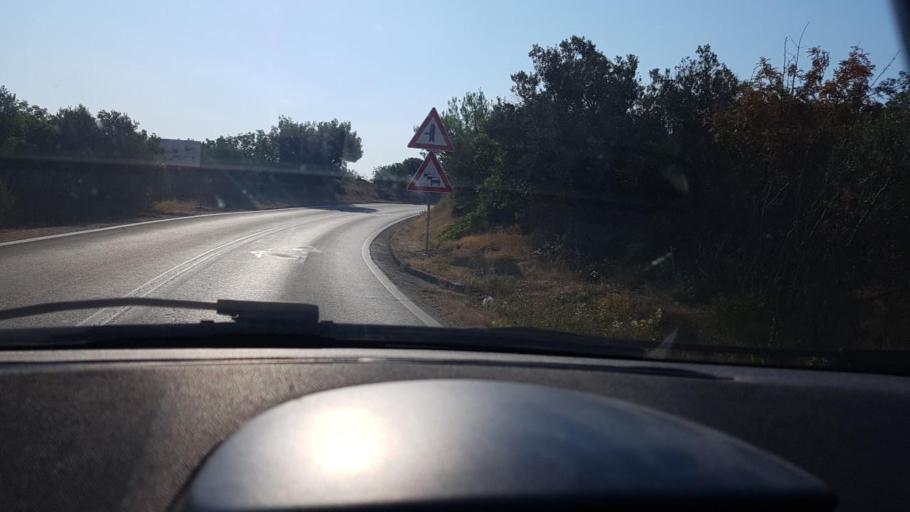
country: HR
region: Sibensko-Kniniska
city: Murter
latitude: 43.8124
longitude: 15.6001
